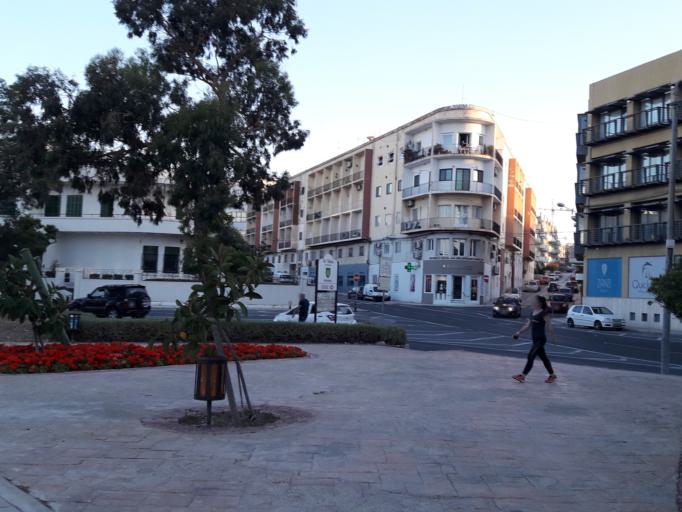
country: MT
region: Ta' Xbiex
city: Ta' Xbiex
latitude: 35.9019
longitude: 14.4949
